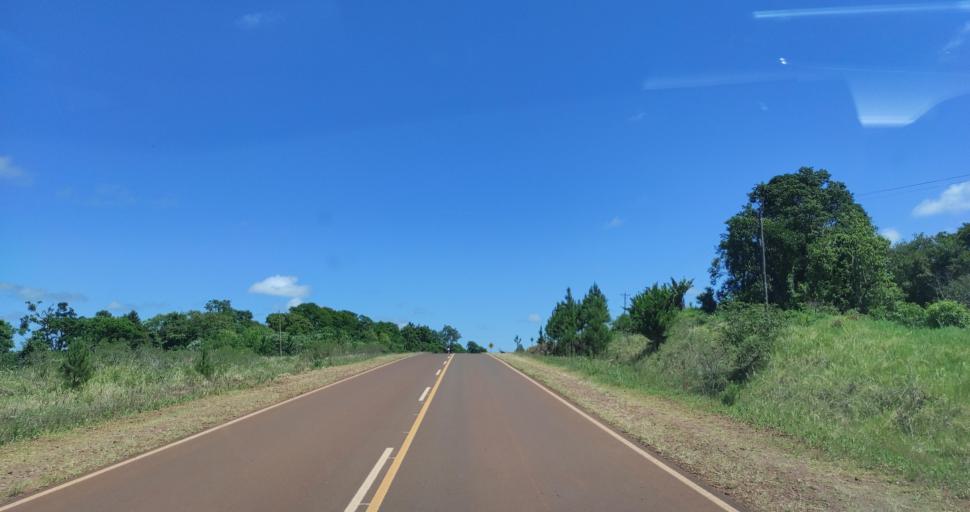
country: AR
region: Misiones
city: Campo Grande
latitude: -27.3230
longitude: -54.8951
